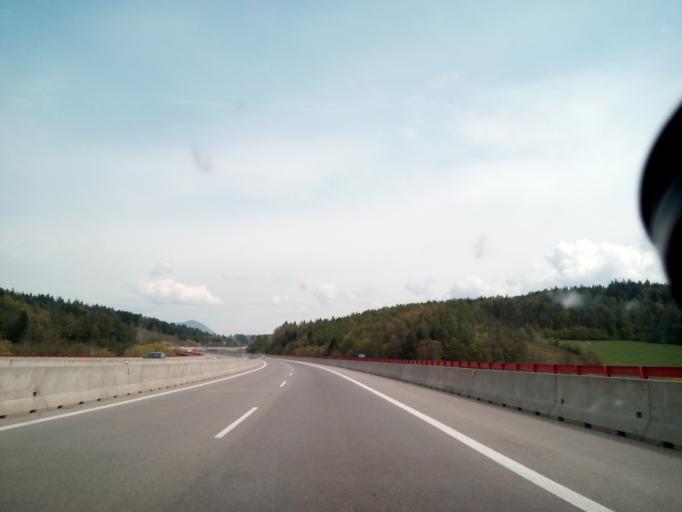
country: SK
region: Trenciansky
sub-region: Okres Povazska Bystrica
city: Povazska Bystrica
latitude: 49.0641
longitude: 18.3833
